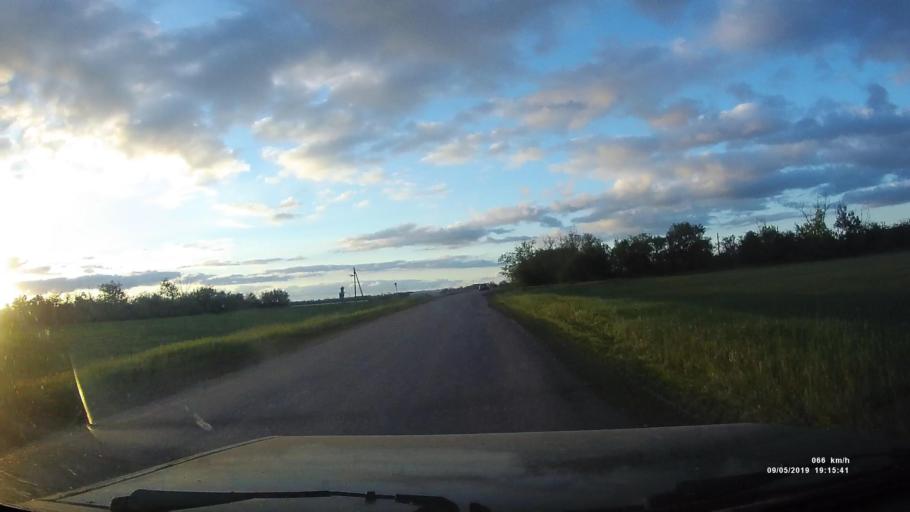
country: RU
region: Krasnodarskiy
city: Kanelovskaya
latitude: 46.7704
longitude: 39.2113
